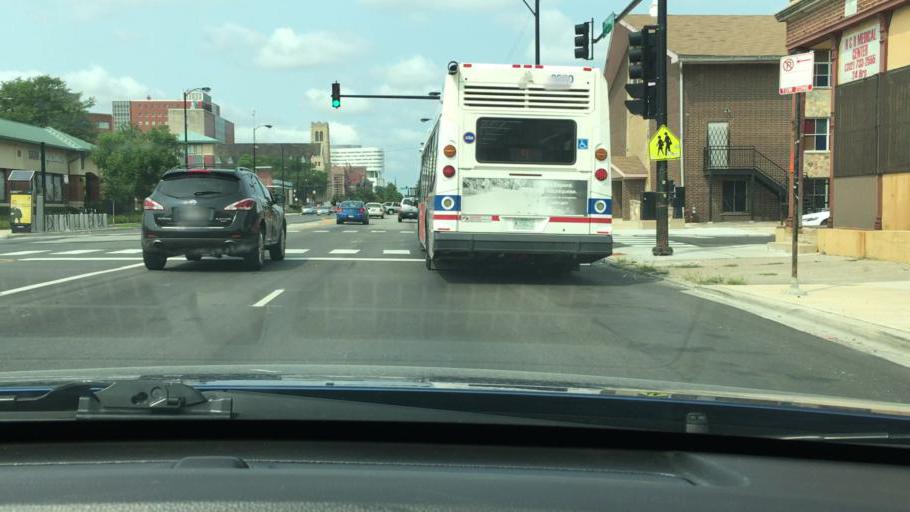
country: US
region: Illinois
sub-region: Cook County
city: Chicago
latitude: 41.8649
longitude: -87.6663
